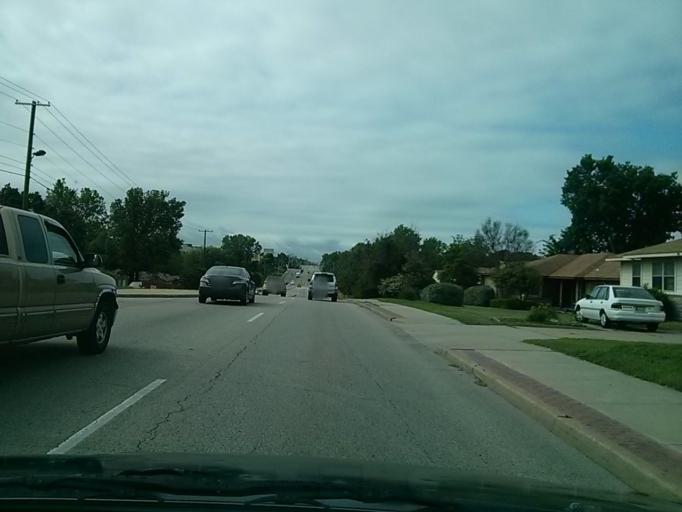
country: US
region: Oklahoma
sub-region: Tulsa County
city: Tulsa
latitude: 36.1096
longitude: -95.9225
